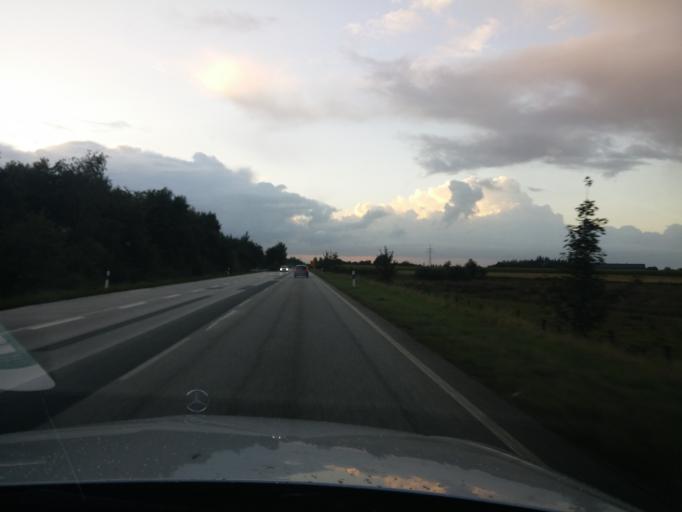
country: DE
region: Schleswig-Holstein
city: Horstedt
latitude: 54.5114
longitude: 9.0734
